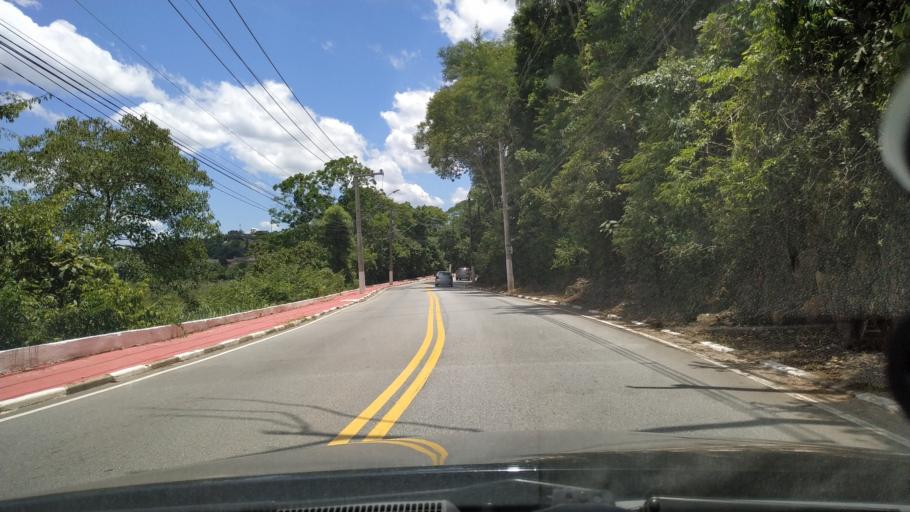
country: BR
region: Sao Paulo
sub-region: Santana De Parnaiba
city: Santana de Parnaiba
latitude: -23.4448
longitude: -46.9068
